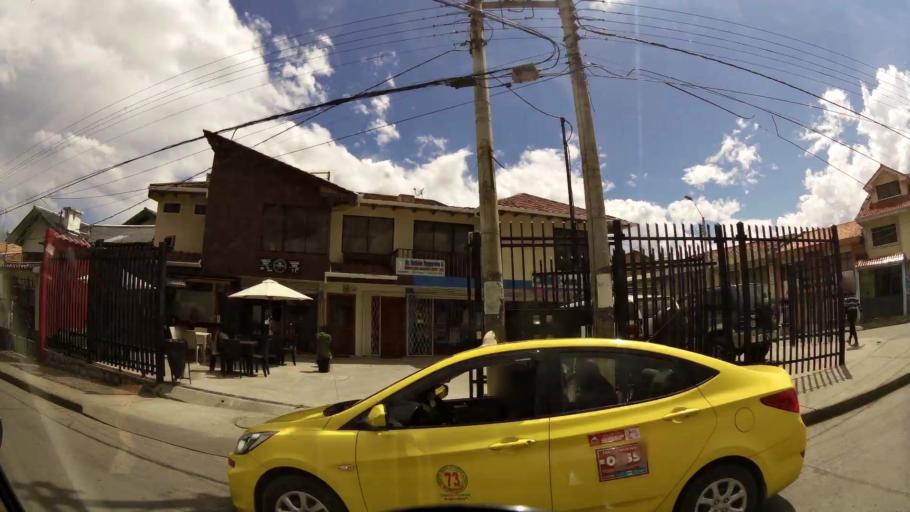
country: EC
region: Azuay
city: Cuenca
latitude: -2.8901
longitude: -78.9976
